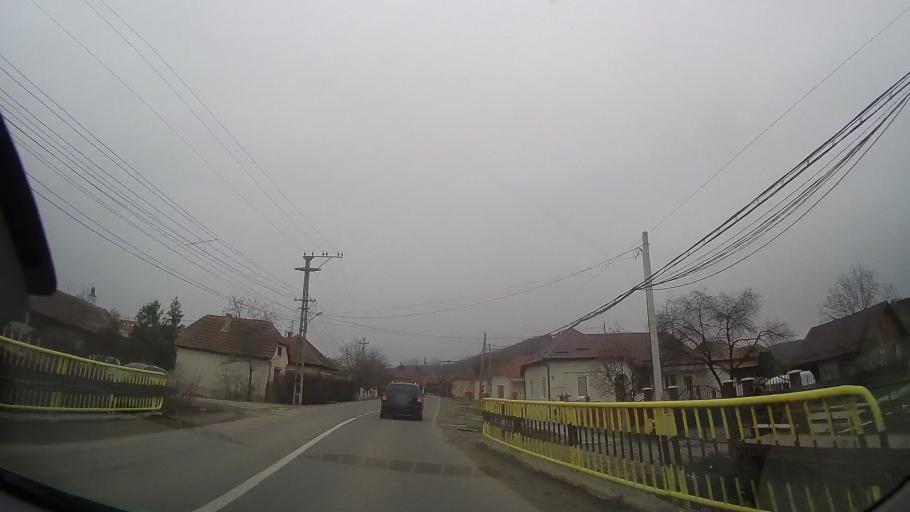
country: RO
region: Mures
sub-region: Comuna Ceausu de Campie
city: Ceausu de Campie
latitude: 46.6137
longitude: 24.5271
